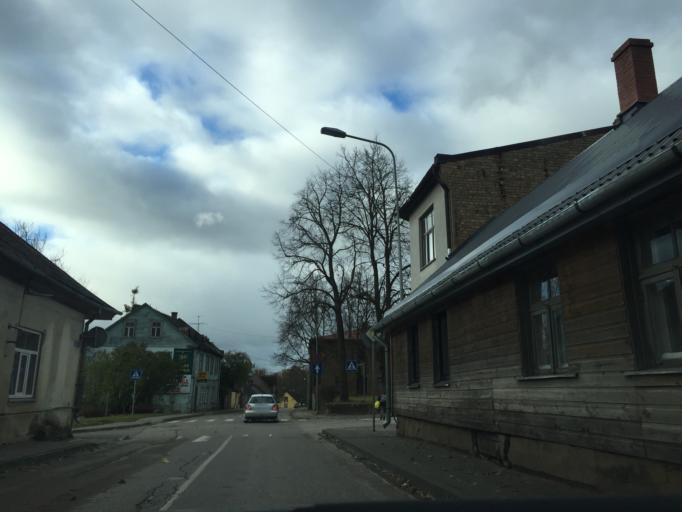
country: LV
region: Tukuma Rajons
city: Tukums
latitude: 56.9669
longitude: 23.1499
